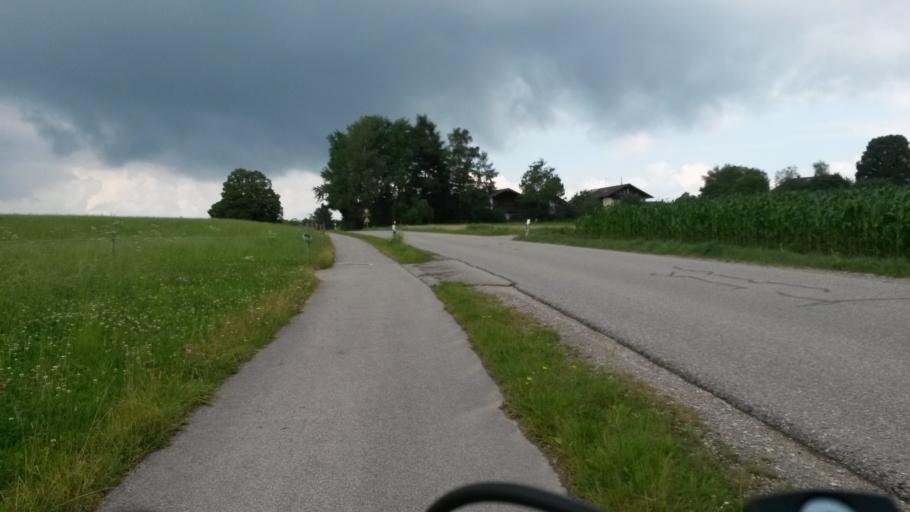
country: DE
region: Bavaria
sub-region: Upper Bavaria
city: Hoslwang
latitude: 47.9635
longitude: 12.3237
